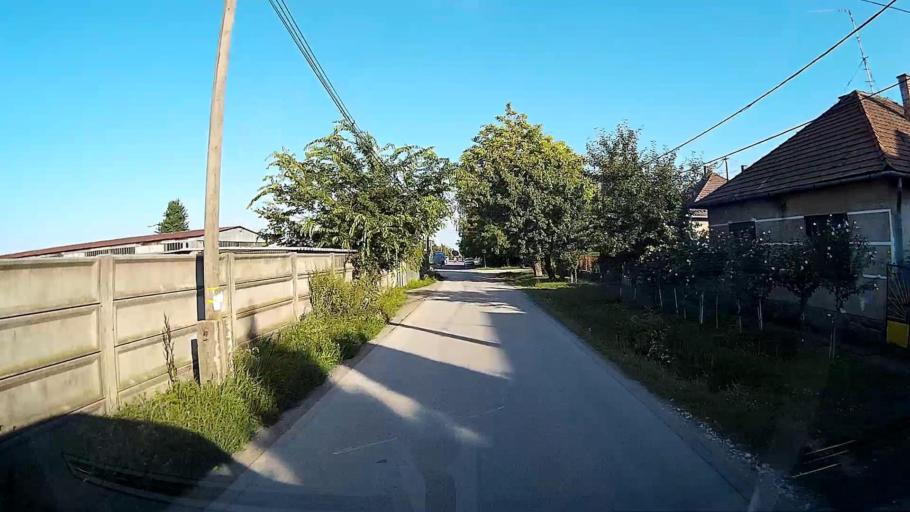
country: HU
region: Pest
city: Tahitotfalu
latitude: 47.7563
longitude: 19.0943
